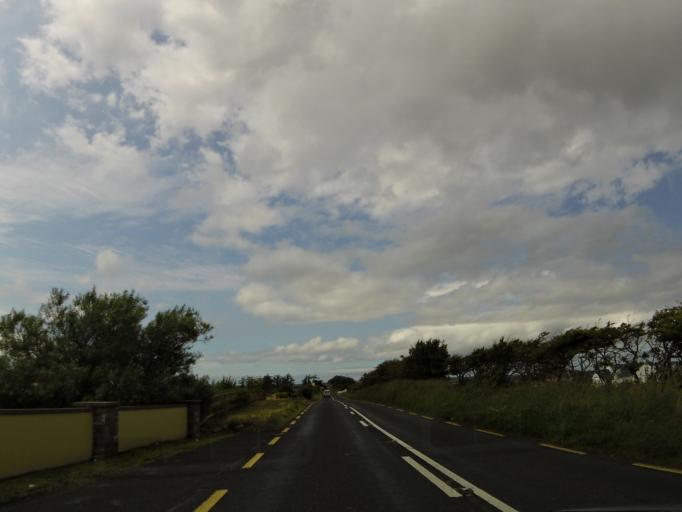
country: IE
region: Munster
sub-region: An Clar
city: Kilrush
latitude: 52.6515
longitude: -9.5155
